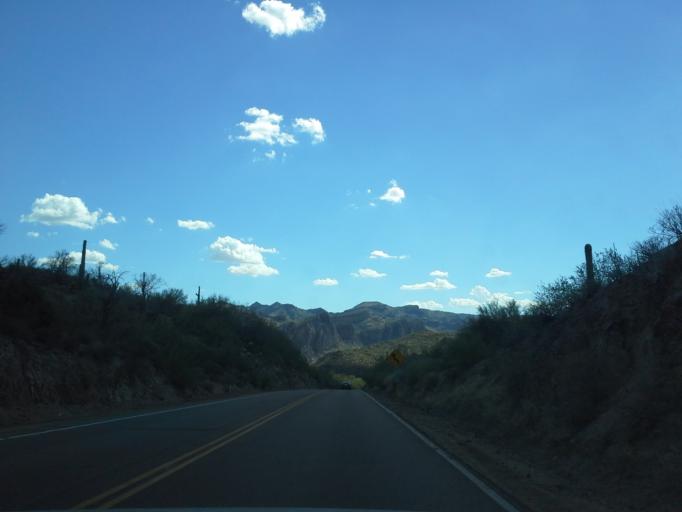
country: US
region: Arizona
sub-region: Pinal County
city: Apache Junction
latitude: 33.5827
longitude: -111.5400
